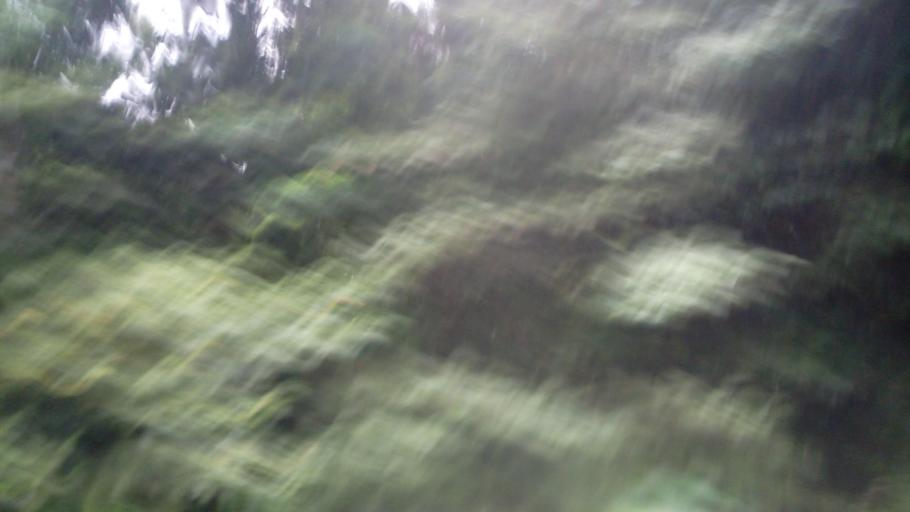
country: AU
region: Queensland
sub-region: Tablelands
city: Ravenshoe
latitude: -17.5950
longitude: 145.7517
